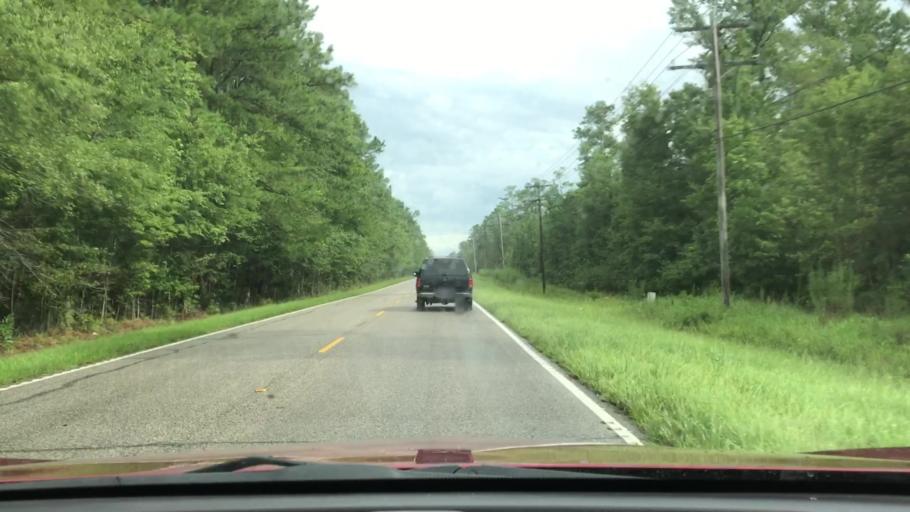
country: US
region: South Carolina
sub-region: Georgetown County
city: Georgetown
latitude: 33.4441
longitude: -79.2777
